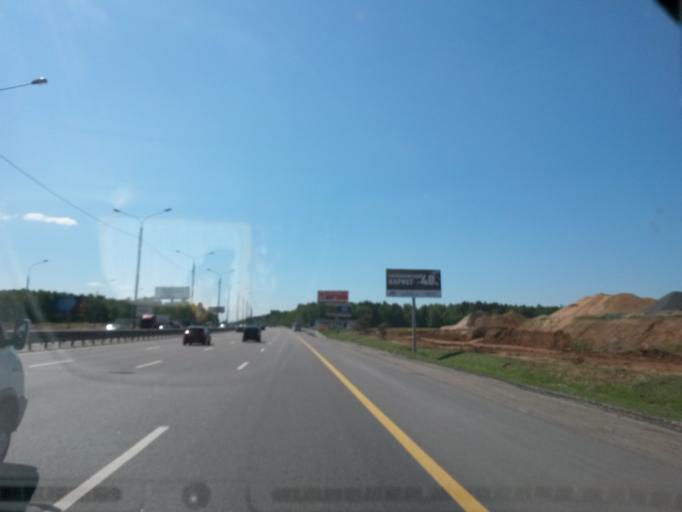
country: RU
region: Moskovskaya
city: Shcherbinka
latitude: 55.5237
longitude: 37.6092
